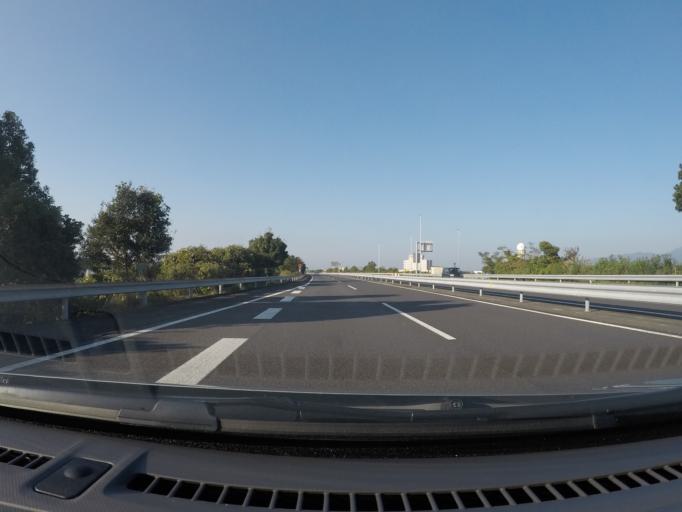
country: JP
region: Kagoshima
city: Kokubu-matsuki
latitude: 31.7904
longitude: 130.7173
